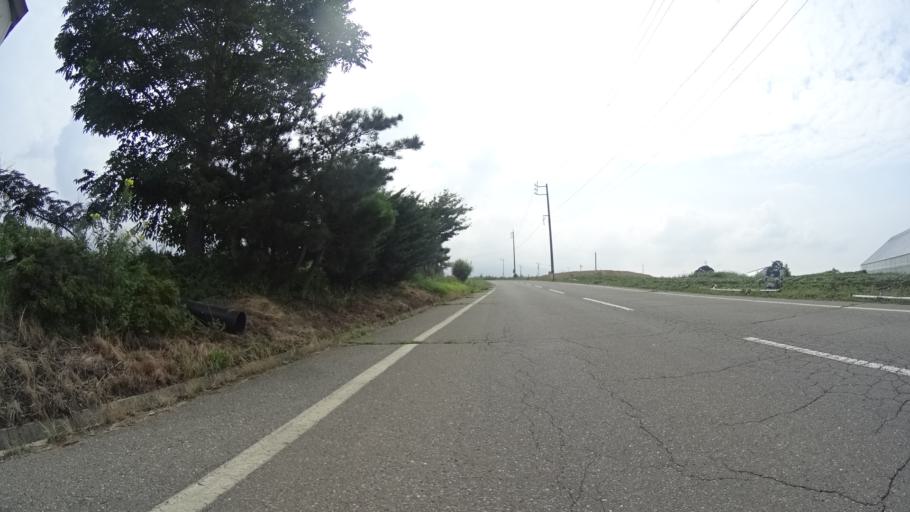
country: JP
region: Nagano
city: Chino
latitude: 35.9441
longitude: 138.2453
